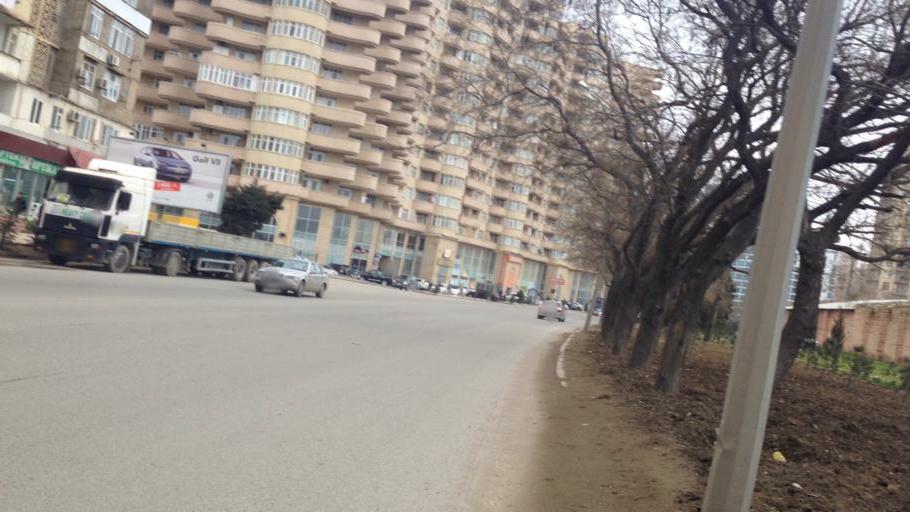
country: AZ
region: Baki
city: Khodzhi-Gasan
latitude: 40.3916
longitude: 49.8154
